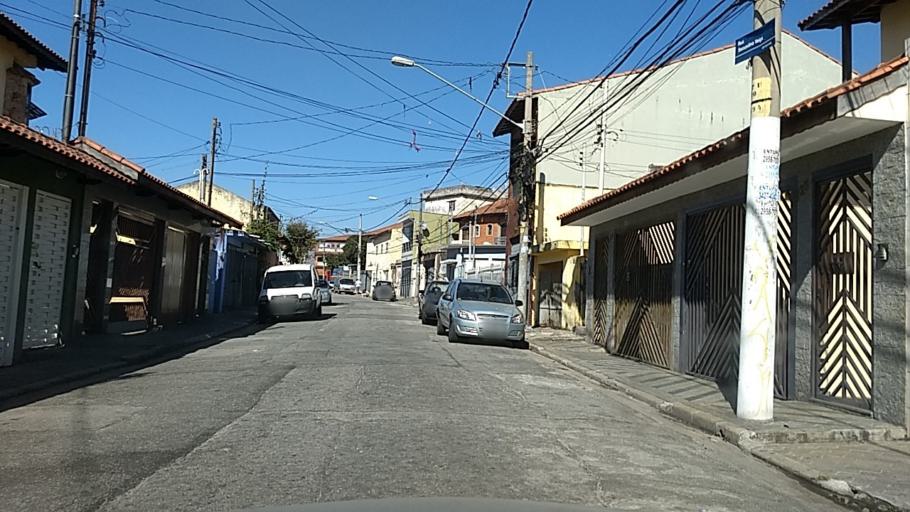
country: BR
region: Sao Paulo
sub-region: Guarulhos
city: Guarulhos
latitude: -23.4981
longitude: -46.5772
